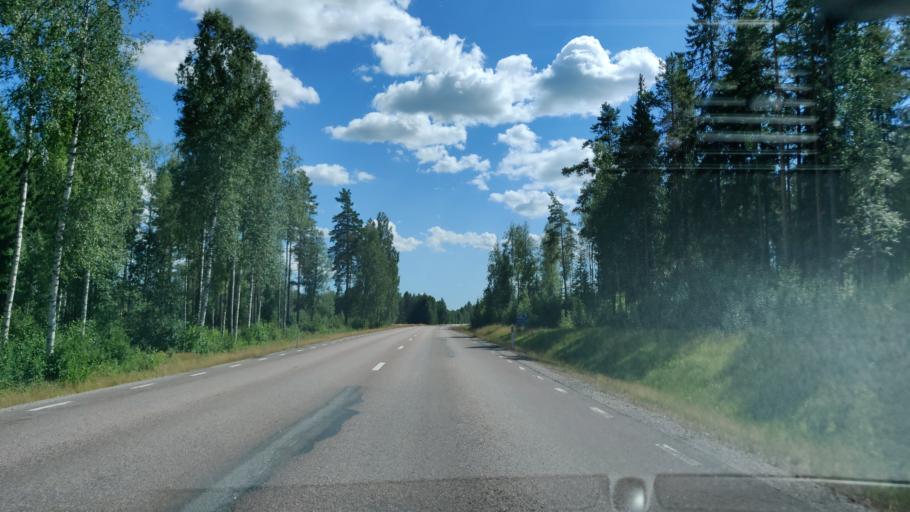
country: SE
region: Vaermland
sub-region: Hagfors Kommun
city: Ekshaerad
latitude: 60.2077
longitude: 13.4886
